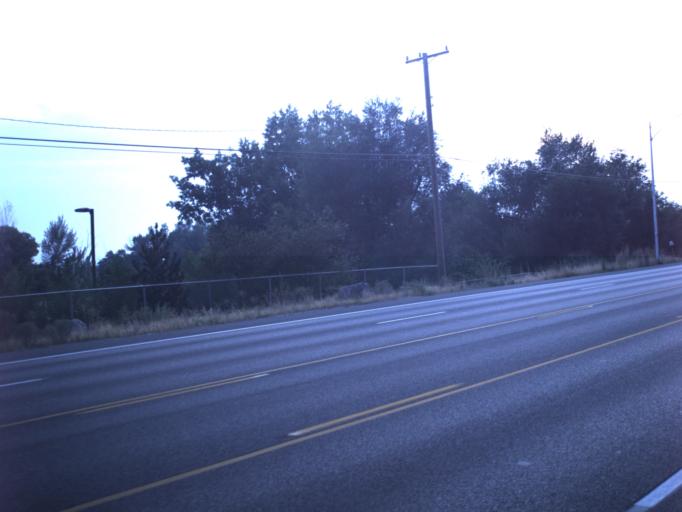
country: US
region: Utah
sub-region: Utah County
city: Springville
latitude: 40.2040
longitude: -111.6248
